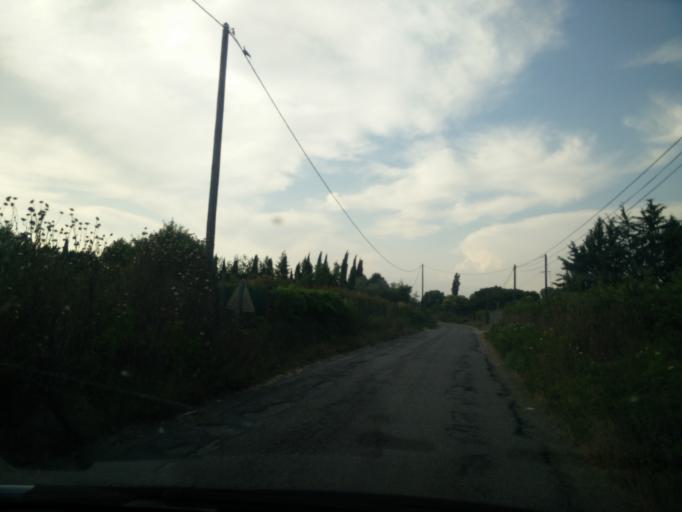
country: FR
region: Languedoc-Roussillon
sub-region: Departement de l'Herault
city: Marsillargues
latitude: 43.6745
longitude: 4.1741
